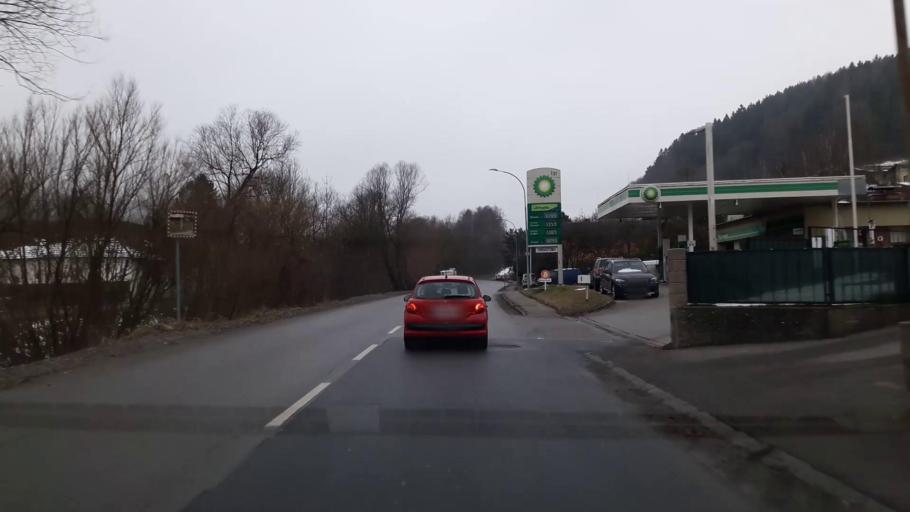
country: AT
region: Lower Austria
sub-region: Politischer Bezirk Neunkirchen
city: Thomasberg
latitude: 47.5678
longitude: 16.0983
